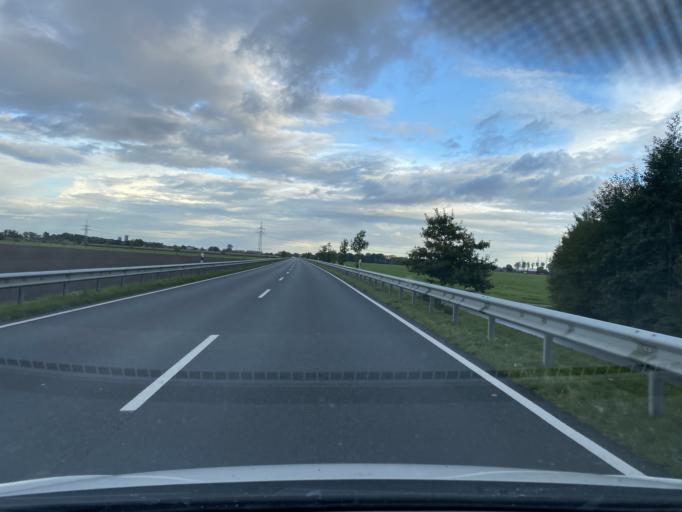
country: DE
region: Lower Saxony
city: Otterndorf
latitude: 53.7967
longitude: 8.8794
